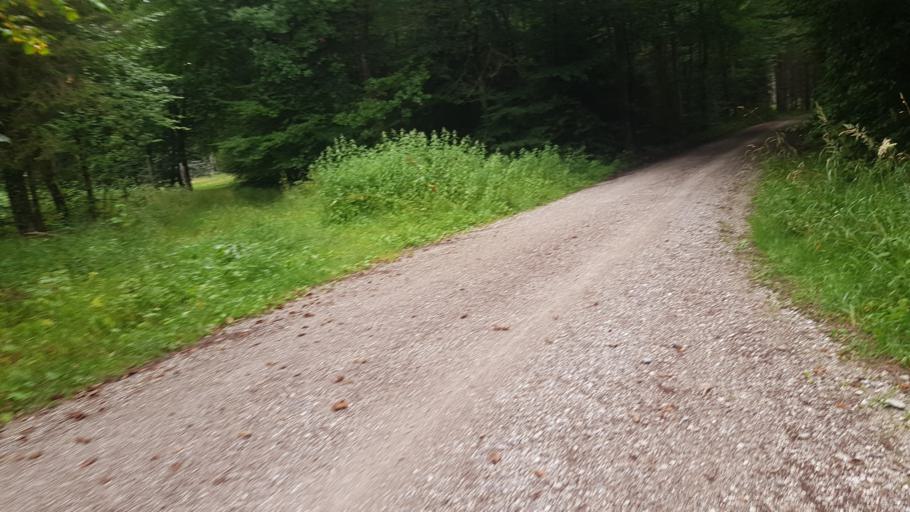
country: DE
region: Bavaria
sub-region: Upper Bavaria
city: Starnberg
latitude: 48.0321
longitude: 11.3397
